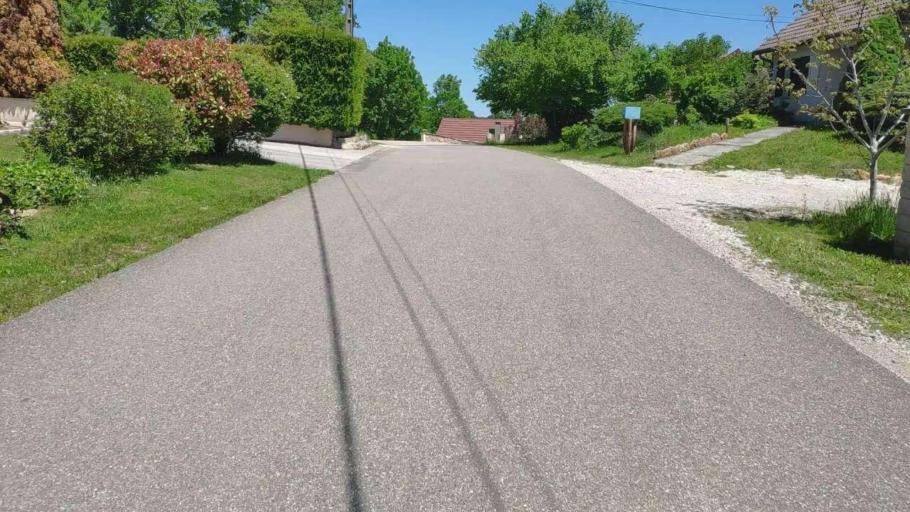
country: FR
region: Franche-Comte
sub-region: Departement du Jura
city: Poligny
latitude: 46.7347
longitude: 5.6909
